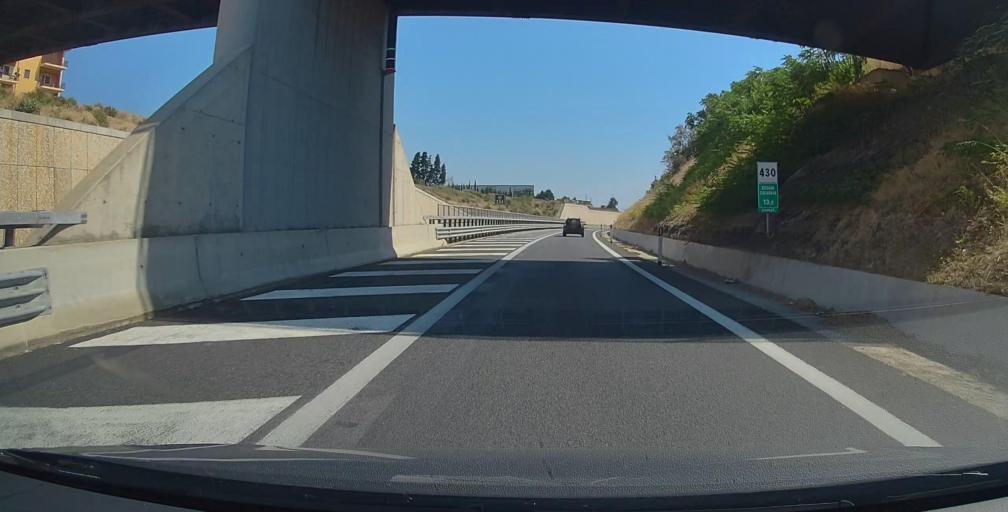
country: IT
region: Calabria
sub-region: Provincia di Reggio Calabria
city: Campo Calabro
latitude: 38.2181
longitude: 15.6479
